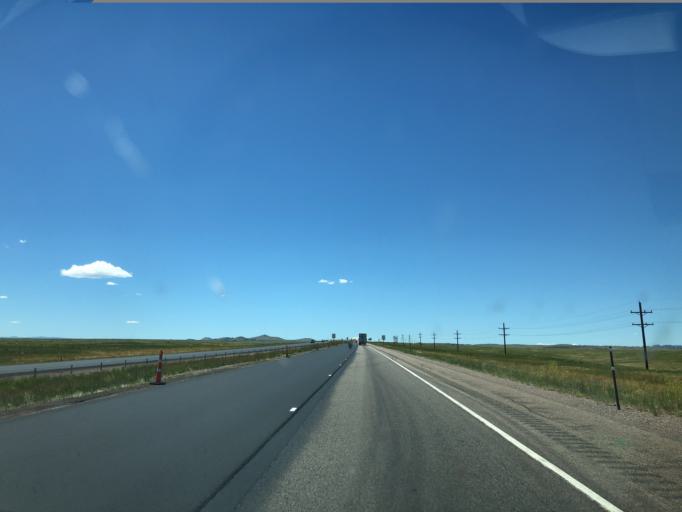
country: US
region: Wyoming
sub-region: Laramie County
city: Cheyenne
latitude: 41.1002
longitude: -105.0803
